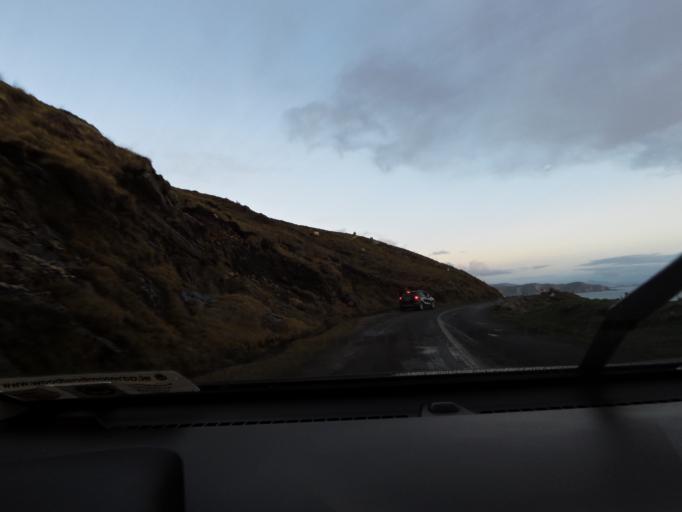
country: IE
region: Connaught
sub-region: Maigh Eo
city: Belmullet
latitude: 53.9699
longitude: -10.1721
